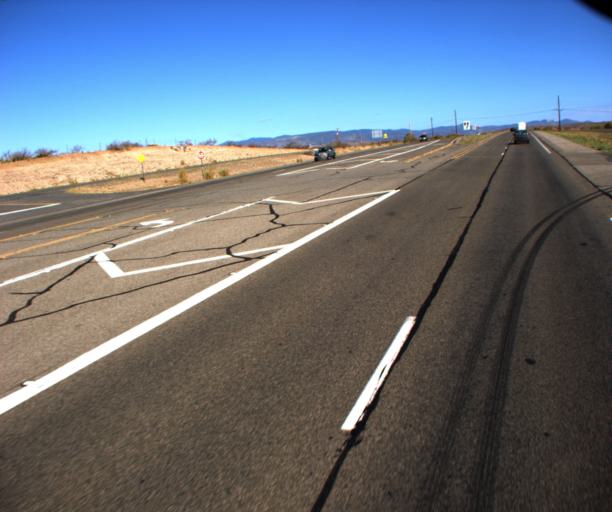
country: US
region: Arizona
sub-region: Yavapai County
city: Spring Valley
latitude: 34.3388
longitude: -112.1334
